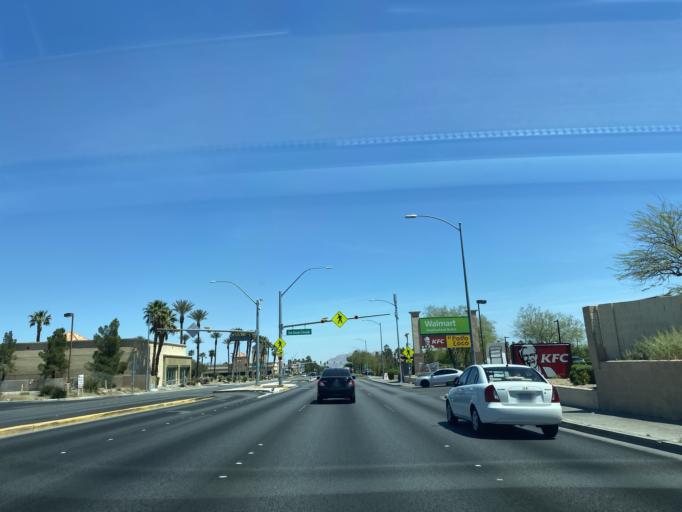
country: US
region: Nevada
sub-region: Clark County
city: Spring Valley
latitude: 36.1957
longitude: -115.2271
